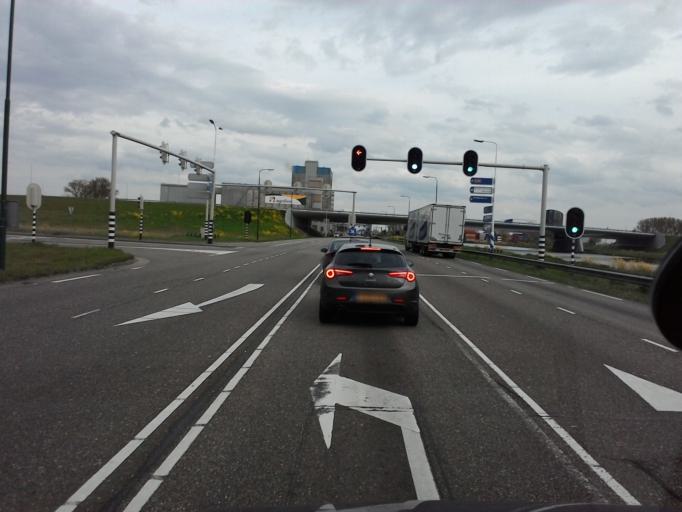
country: NL
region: North Brabant
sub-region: Gemeente Veghel
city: Eerde
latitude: 51.6253
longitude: 5.5010
